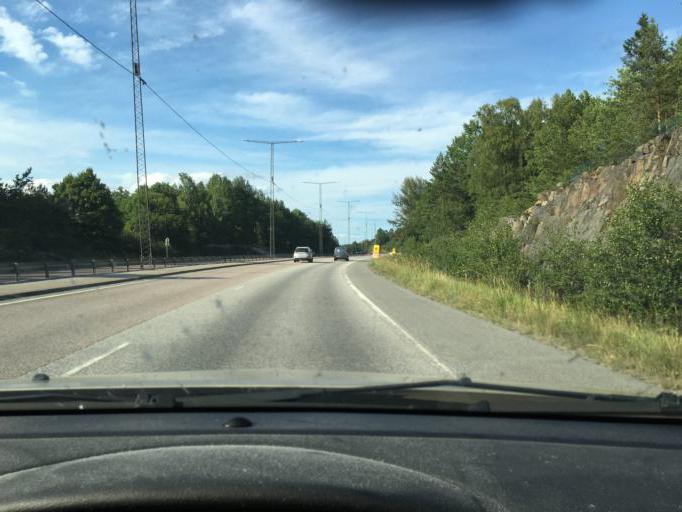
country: SE
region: Stockholm
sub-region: Nacka Kommun
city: Boo
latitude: 59.3173
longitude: 18.2551
